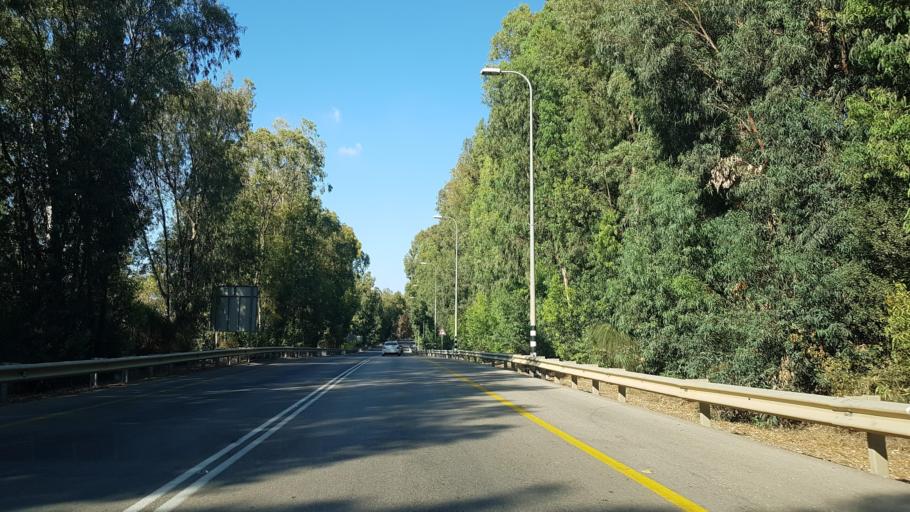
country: PS
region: West Bank
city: Tulkarm
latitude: 32.3521
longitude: 35.0140
